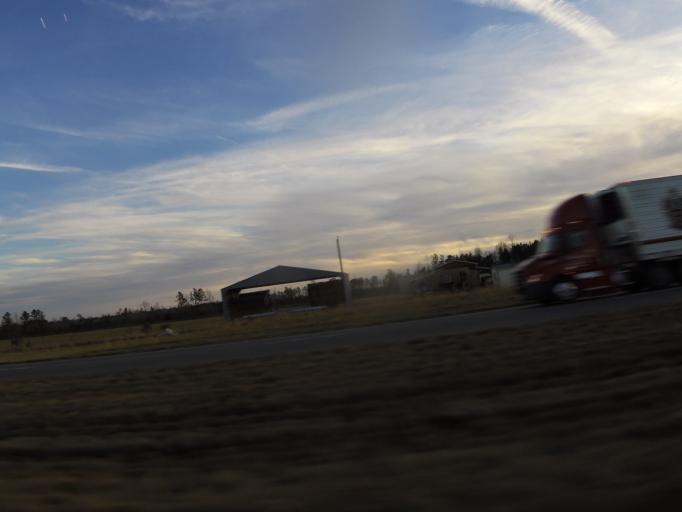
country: US
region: Virginia
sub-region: Southampton County
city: Courtland
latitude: 36.6825
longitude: -77.0069
